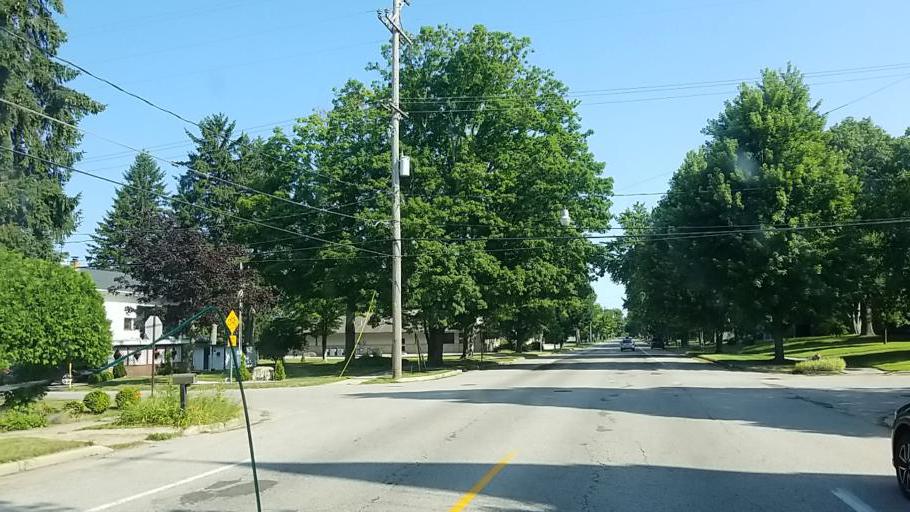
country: US
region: Michigan
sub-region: Muskegon County
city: Whitehall
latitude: 43.3962
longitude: -86.3478
